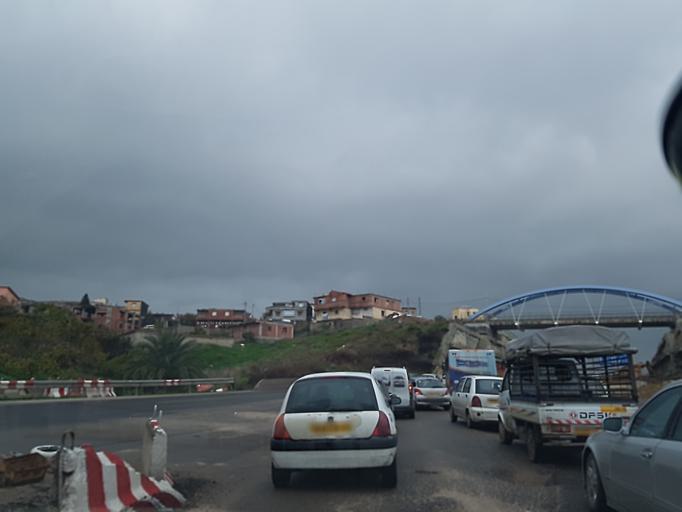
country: DZ
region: Boumerdes
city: Ouled Moussa
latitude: 36.6763
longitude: 3.3787
